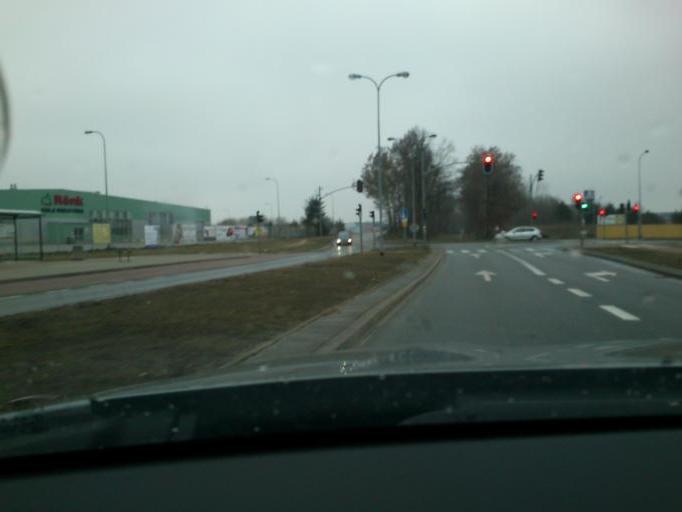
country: PL
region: Pomeranian Voivodeship
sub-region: Gdynia
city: Wielki Kack
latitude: 54.4139
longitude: 18.4806
